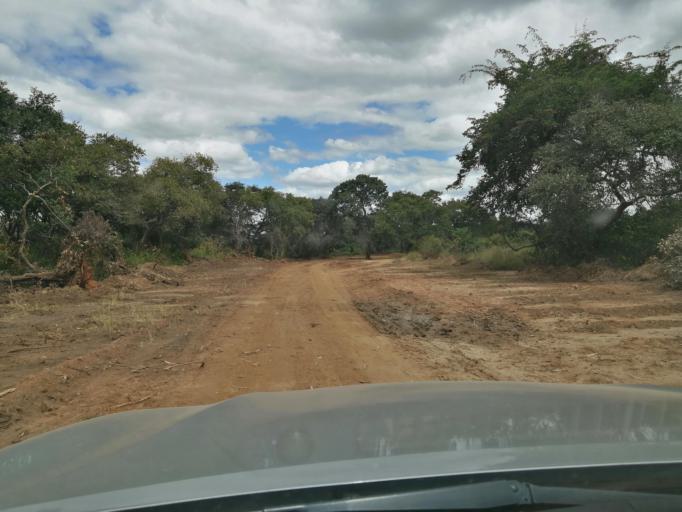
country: ZM
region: Central
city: Mumbwa
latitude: -14.5900
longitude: 27.1936
